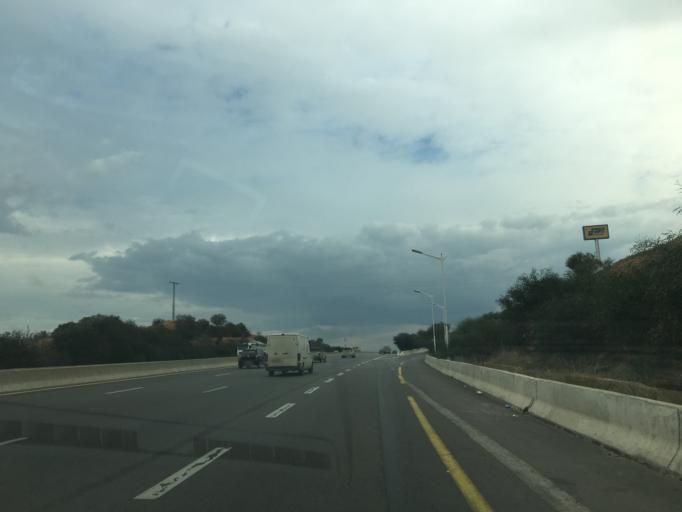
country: DZ
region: Bouira
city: Bouira
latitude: 36.3120
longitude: 4.0582
